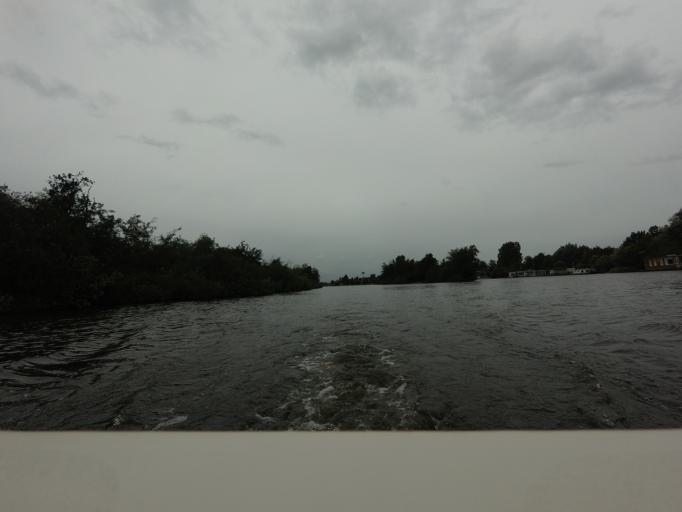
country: NL
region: Friesland
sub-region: Gemeente Tytsjerksteradiel
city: Garyp
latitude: 53.1215
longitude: 5.9432
